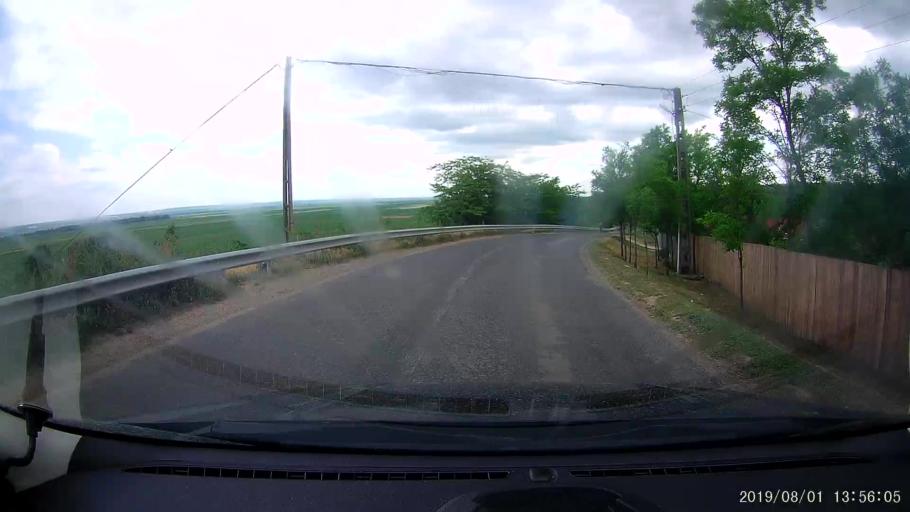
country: RO
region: Galati
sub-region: Comuna Vladesti
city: Vladesti
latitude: 45.8082
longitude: 28.0857
